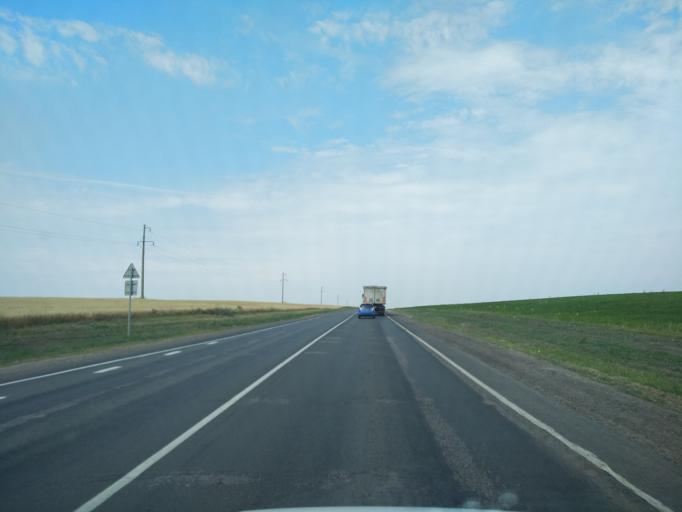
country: RU
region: Voronezj
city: Orlovo
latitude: 51.6820
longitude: 39.5701
